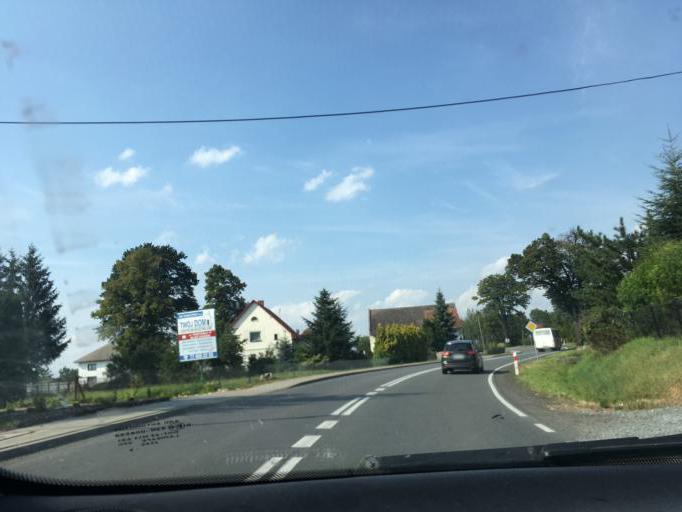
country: PL
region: Opole Voivodeship
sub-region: Powiat prudnicki
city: Prudnik
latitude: 50.3436
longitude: 17.5588
